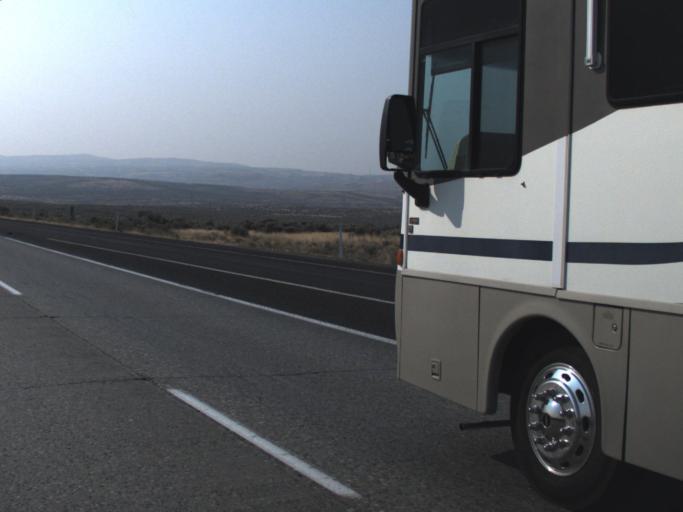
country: US
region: Washington
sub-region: Kittitas County
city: Kittitas
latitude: 46.8404
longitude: -120.3742
